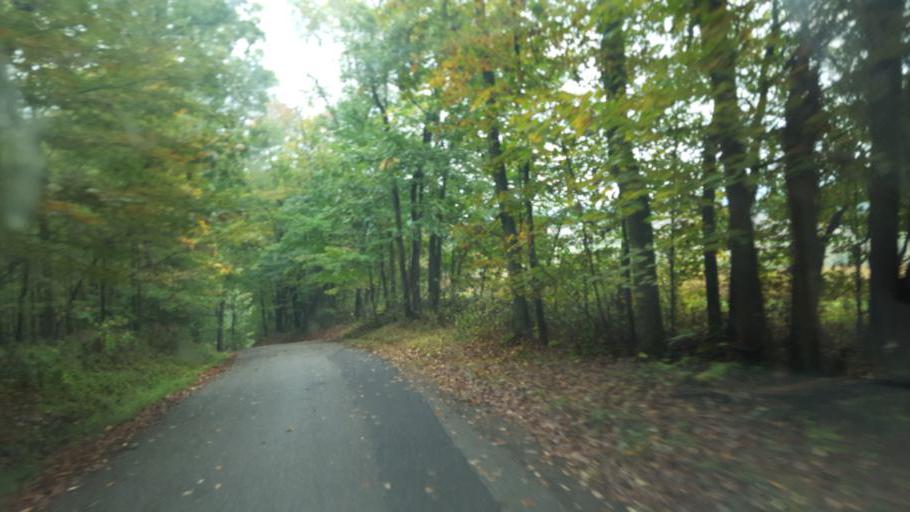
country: US
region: Ohio
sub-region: Ashland County
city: Loudonville
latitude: 40.5621
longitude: -82.2926
